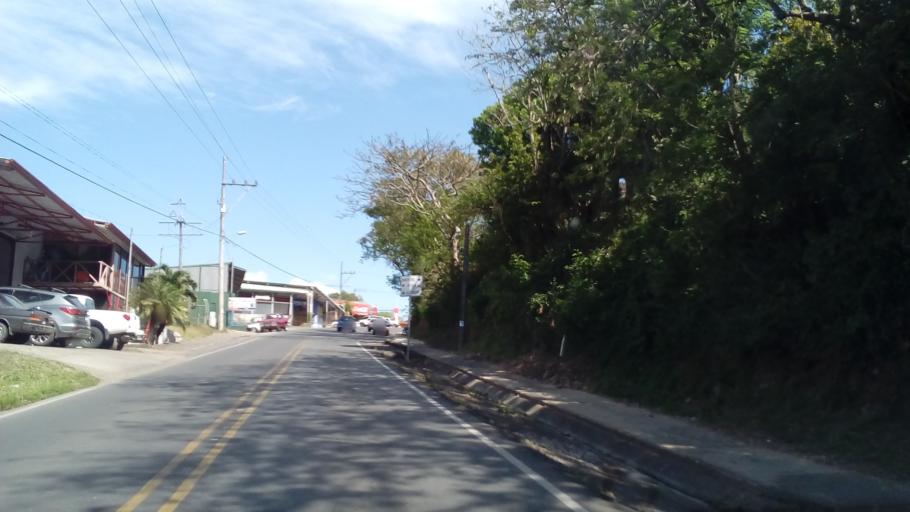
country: CR
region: Guanacaste
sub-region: Canton de Tilaran
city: Tilaran
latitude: 10.4746
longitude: -84.9671
